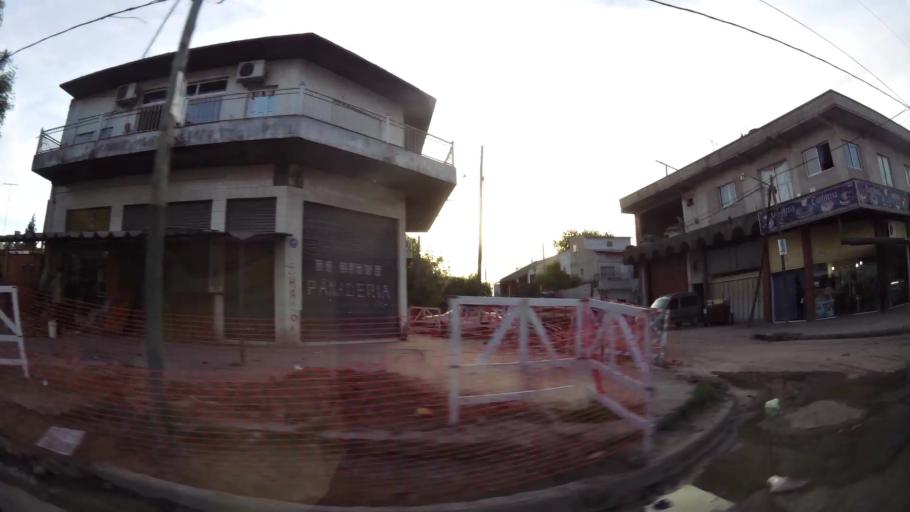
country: AR
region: Buenos Aires
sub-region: Partido de Almirante Brown
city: Adrogue
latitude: -34.7820
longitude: -58.3179
